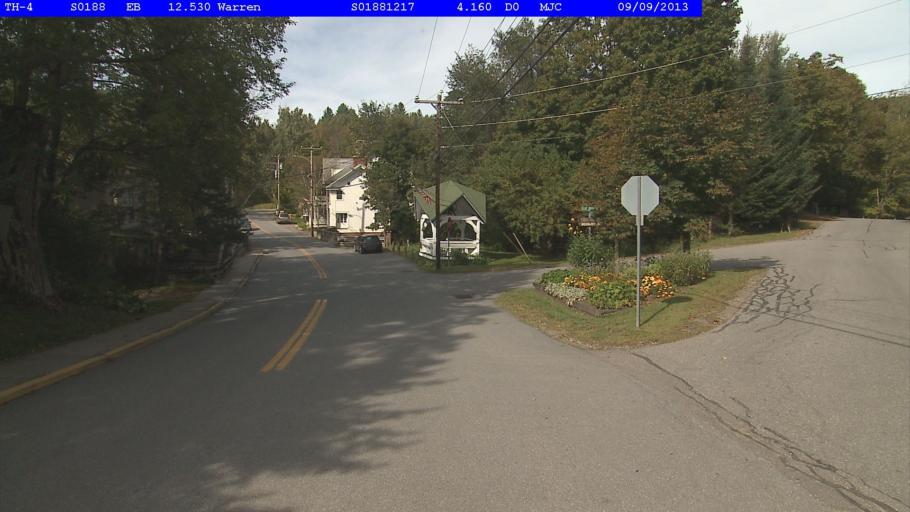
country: US
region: Vermont
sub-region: Washington County
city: Northfield
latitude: 44.1138
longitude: -72.8557
